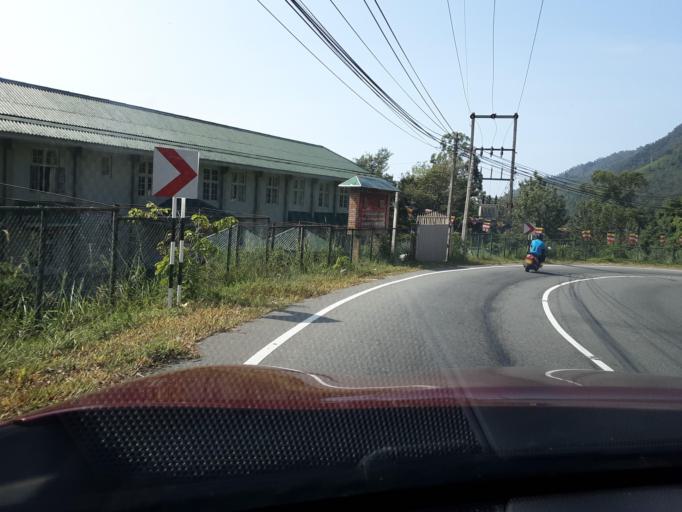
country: LK
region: Uva
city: Badulla
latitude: 6.9510
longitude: 81.1255
